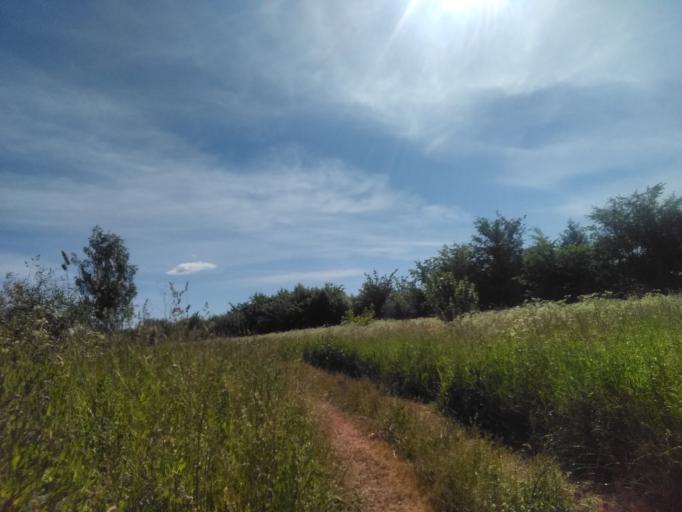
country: RU
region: Udmurtiya
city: Khokhryaki
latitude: 56.8540
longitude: 53.4060
